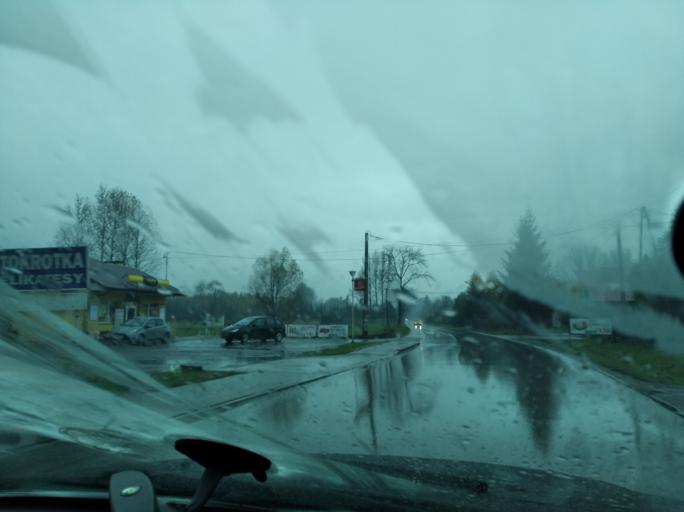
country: PL
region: Subcarpathian Voivodeship
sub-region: Powiat lancucki
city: Kraczkowa
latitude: 50.0393
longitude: 22.1911
